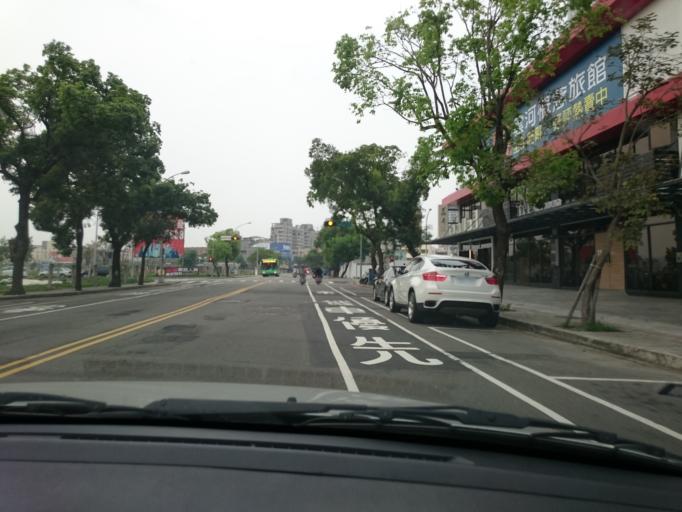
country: TW
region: Taiwan
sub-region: Taichung City
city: Taichung
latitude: 24.1591
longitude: 120.6340
